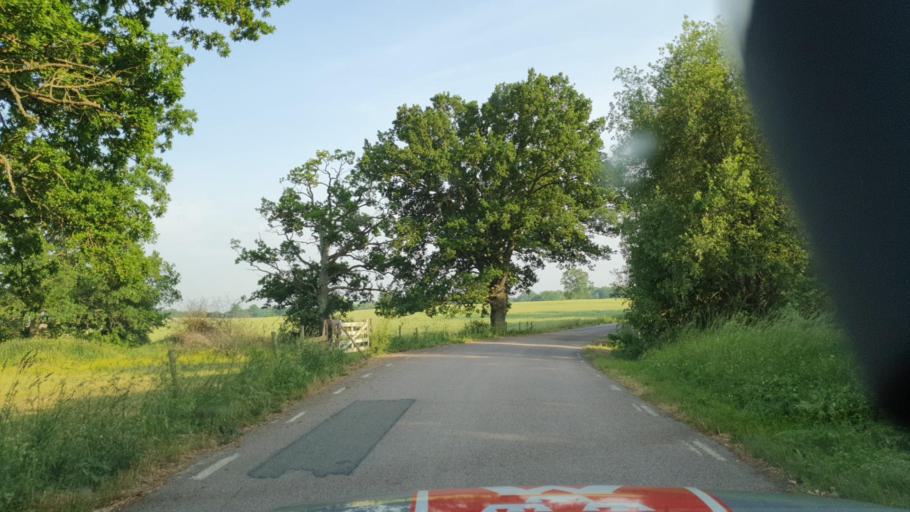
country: SE
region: Kalmar
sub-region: Kalmar Kommun
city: Ljungbyholm
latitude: 56.5243
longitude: 16.1428
